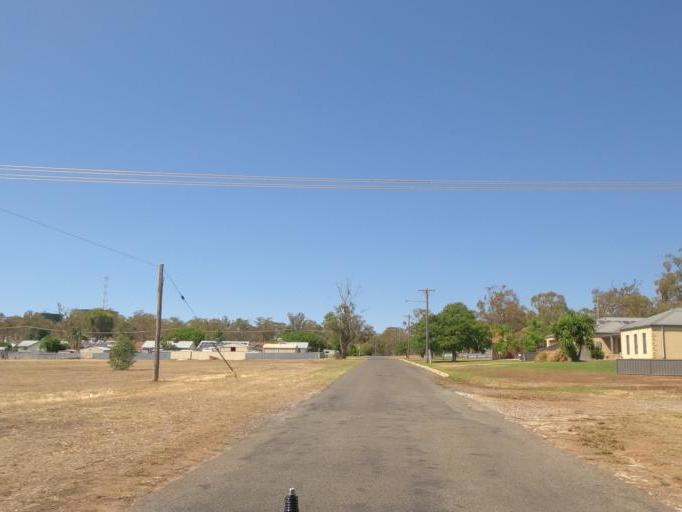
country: AU
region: New South Wales
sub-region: Corowa Shire
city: Mulwala
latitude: -35.9929
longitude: 145.9954
